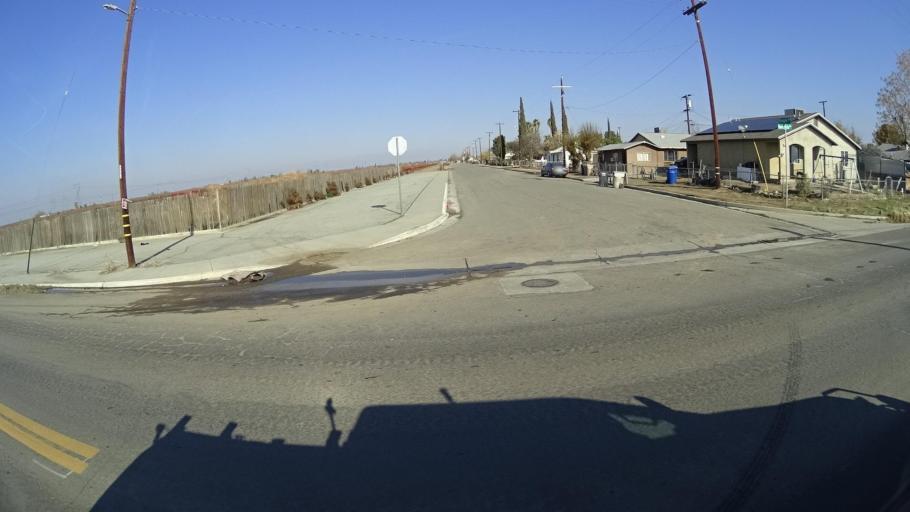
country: US
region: California
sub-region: Kern County
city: Weedpatch
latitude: 35.2376
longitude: -118.9193
